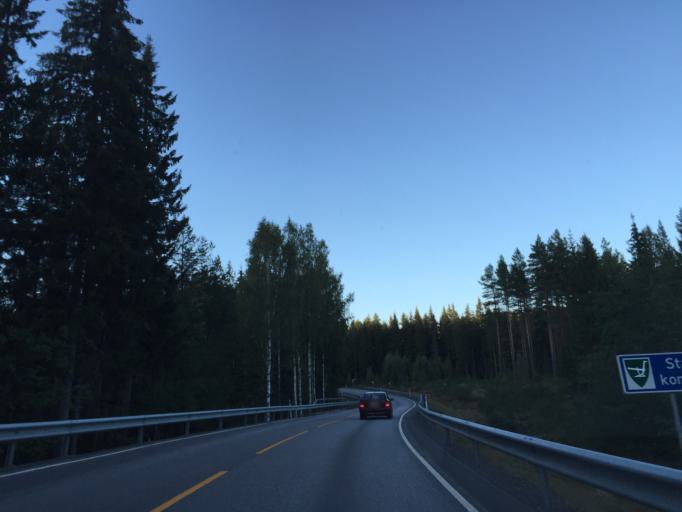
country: NO
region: Hedmark
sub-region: Nord-Odal
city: Sand
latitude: 60.5164
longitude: 11.5098
